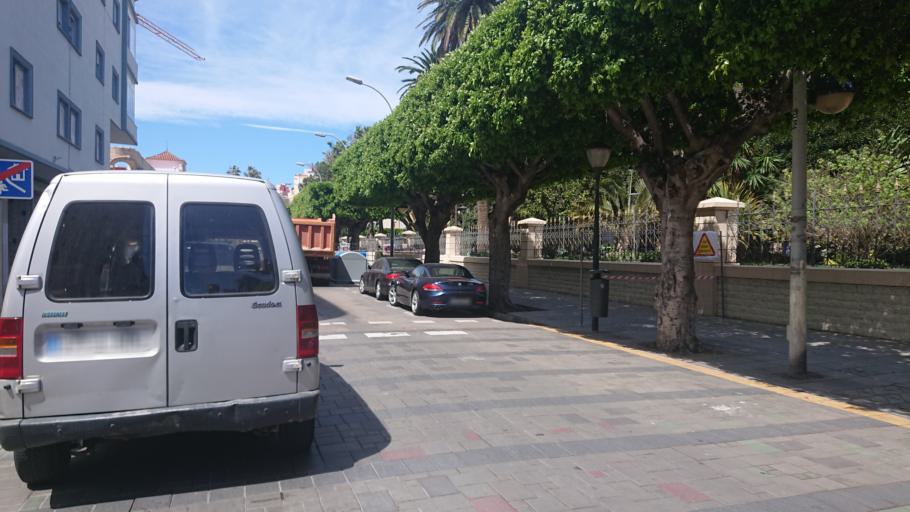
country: ES
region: Melilla
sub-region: Melilla
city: Melilla
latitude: 35.2915
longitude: -2.9426
